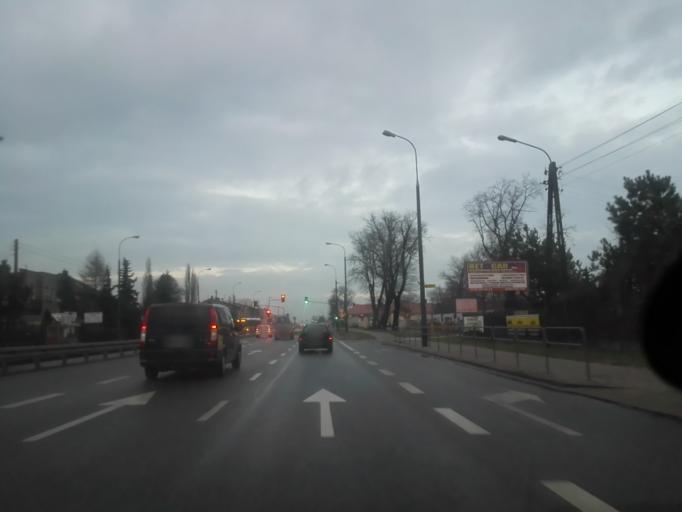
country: PL
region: Masovian Voivodeship
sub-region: Powiat wolominski
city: Marki
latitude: 52.3382
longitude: 21.1176
